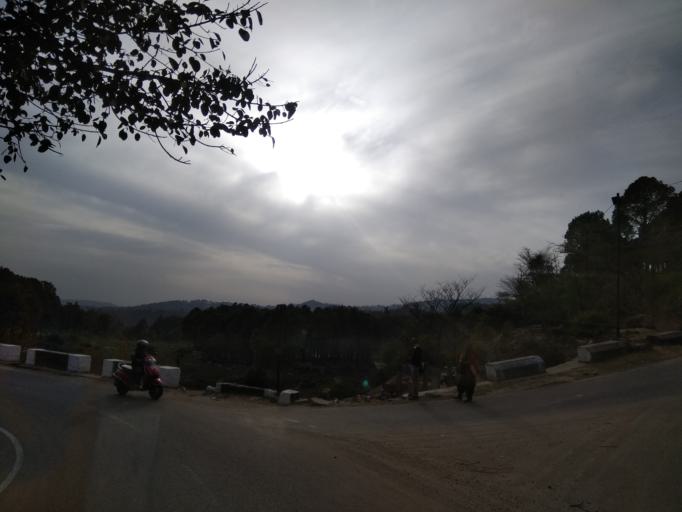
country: IN
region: Himachal Pradesh
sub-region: Kangra
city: Palampur
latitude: 32.1109
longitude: 76.4874
